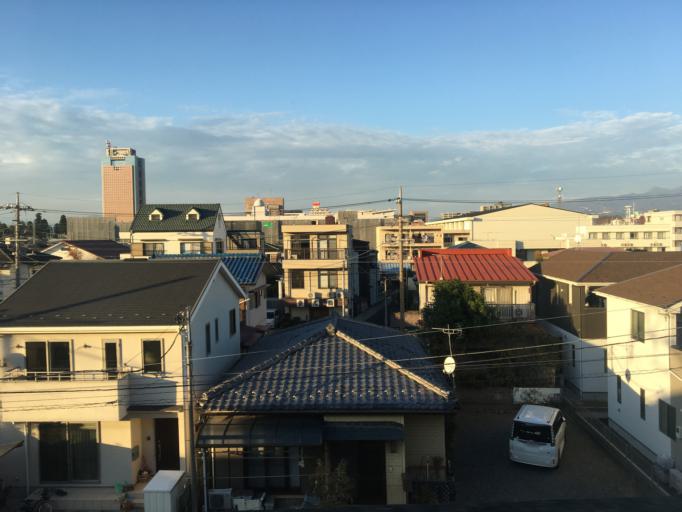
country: JP
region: Gunma
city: Maebashi-shi
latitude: 36.3825
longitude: 139.0656
